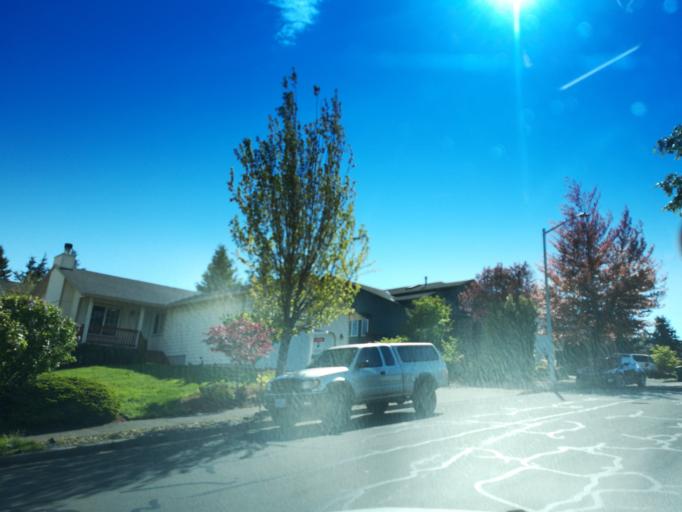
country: US
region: Oregon
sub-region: Multnomah County
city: Troutdale
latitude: 45.5348
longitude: -122.3847
